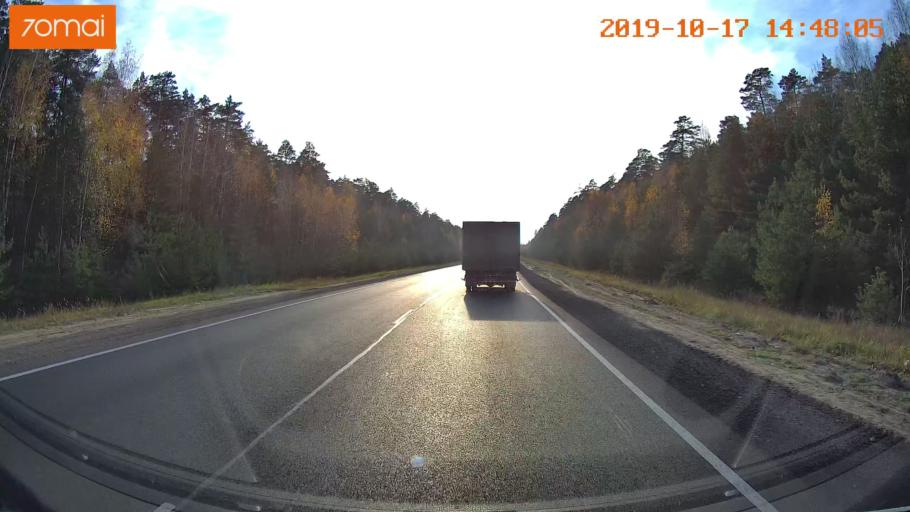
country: RU
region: Rjazan
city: Solotcha
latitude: 54.7630
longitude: 39.8537
